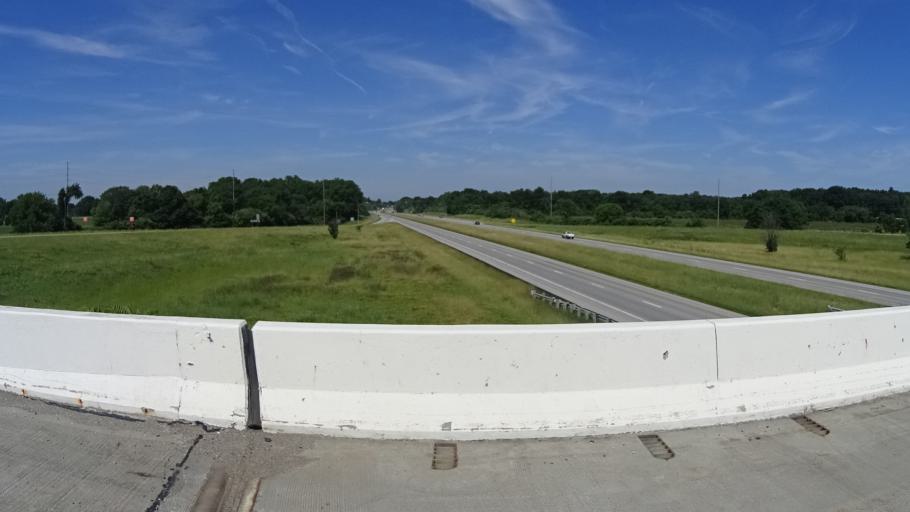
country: US
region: Ohio
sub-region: Erie County
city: Huron
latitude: 41.3677
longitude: -82.4944
